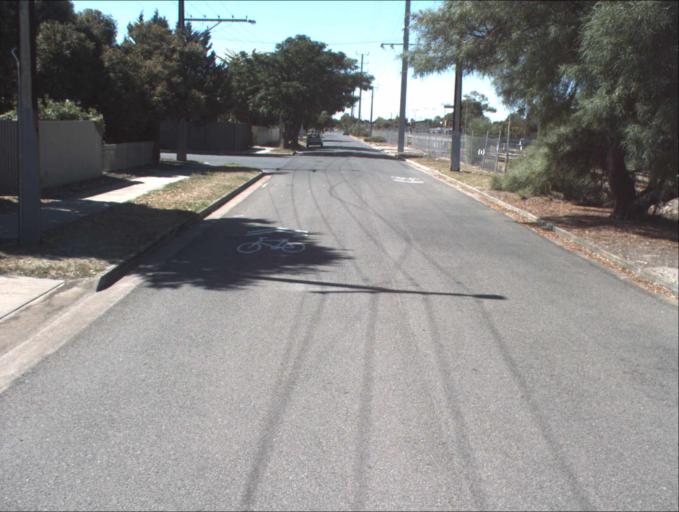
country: AU
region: South Australia
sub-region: Port Adelaide Enfield
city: Birkenhead
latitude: -34.8071
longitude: 138.4988
